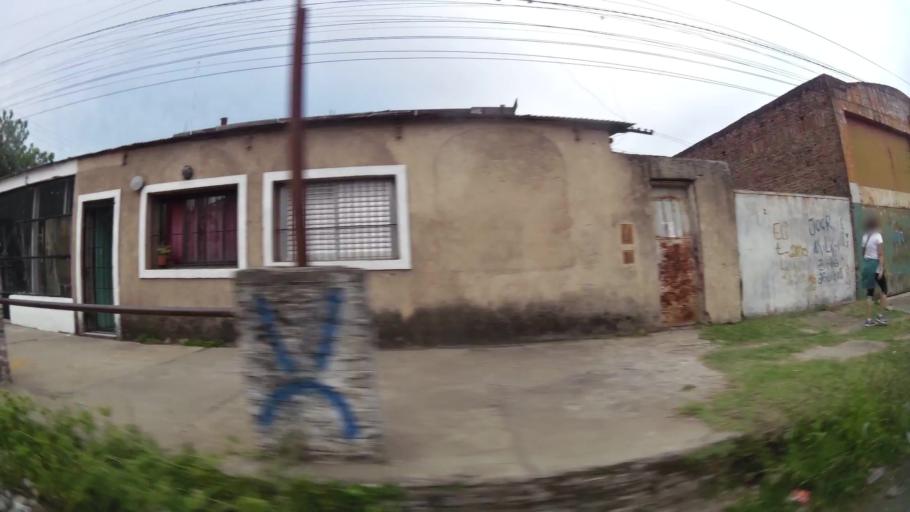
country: AR
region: Santa Fe
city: Granadero Baigorria
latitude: -32.8939
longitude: -60.7096
